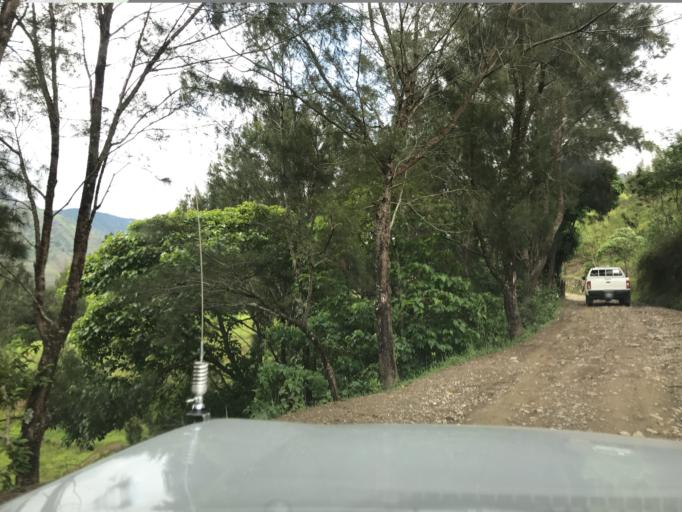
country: TL
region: Aileu
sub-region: Aileu Villa
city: Aileu
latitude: -8.8522
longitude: 125.5859
